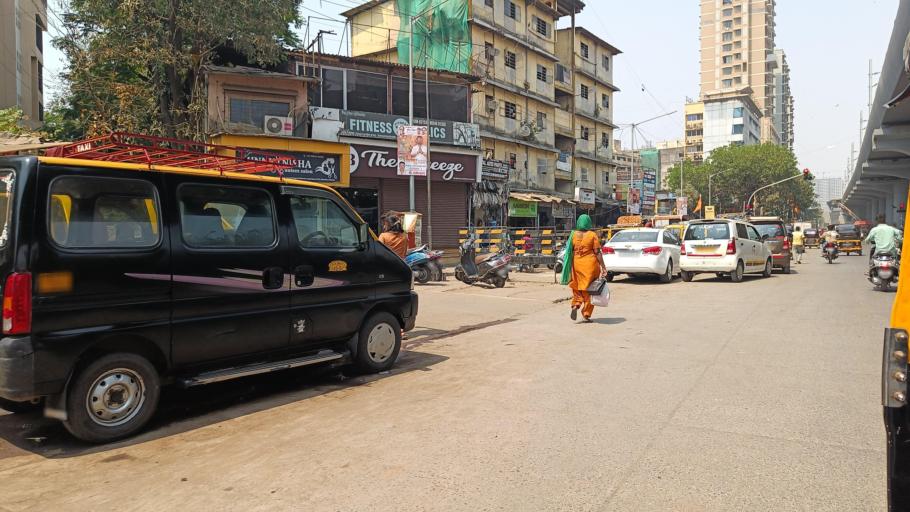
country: IN
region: Maharashtra
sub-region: Mumbai Suburban
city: Powai
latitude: 19.1481
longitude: 72.8363
